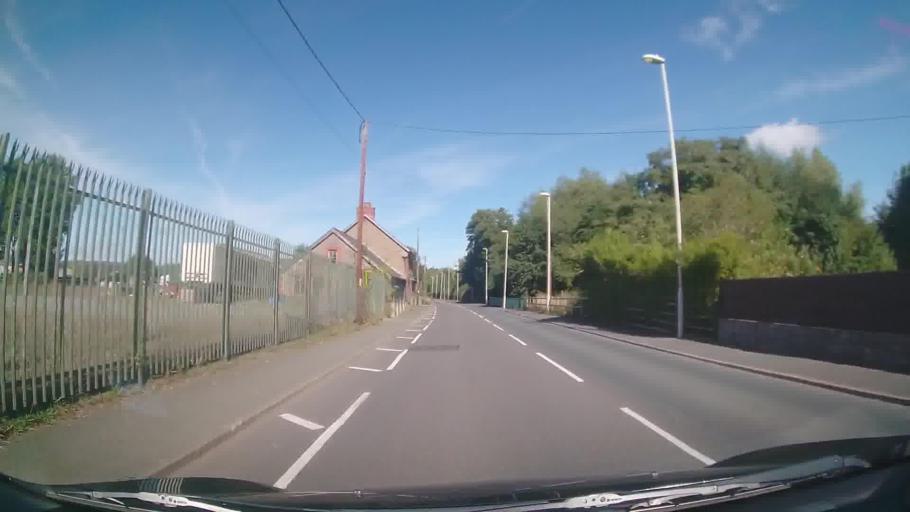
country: GB
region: Wales
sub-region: Sir Powys
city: Hay
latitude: 51.9991
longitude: -3.2343
